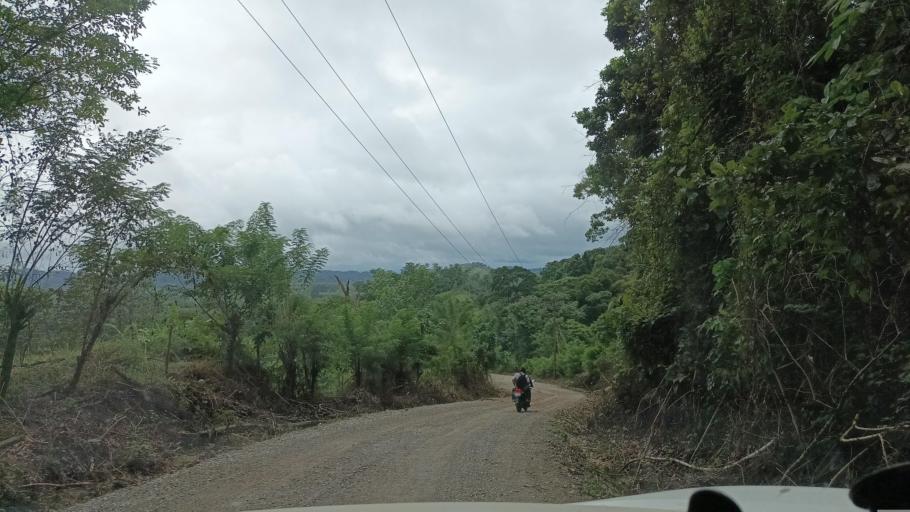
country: MX
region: Veracruz
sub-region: Uxpanapa
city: Poblado 10
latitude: 17.4176
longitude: -94.4175
